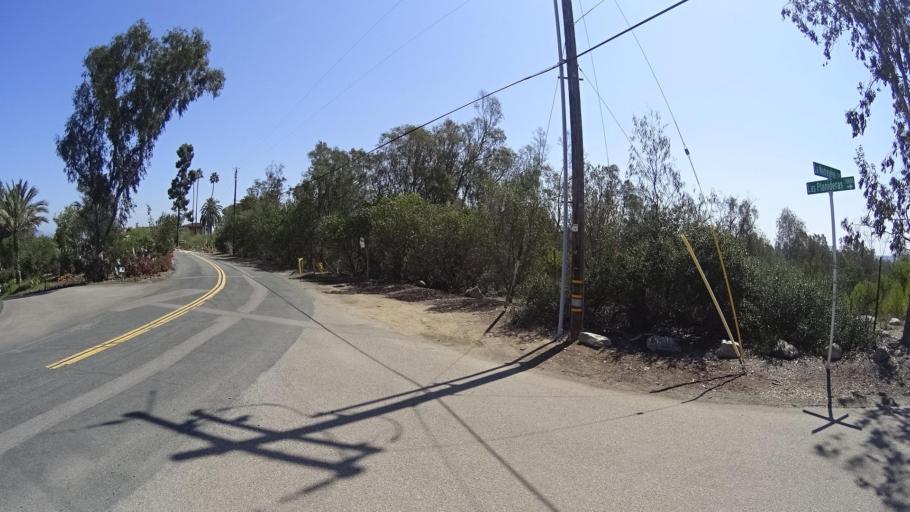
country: US
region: California
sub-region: San Diego County
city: Rancho Santa Fe
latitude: 32.9997
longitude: -117.2211
